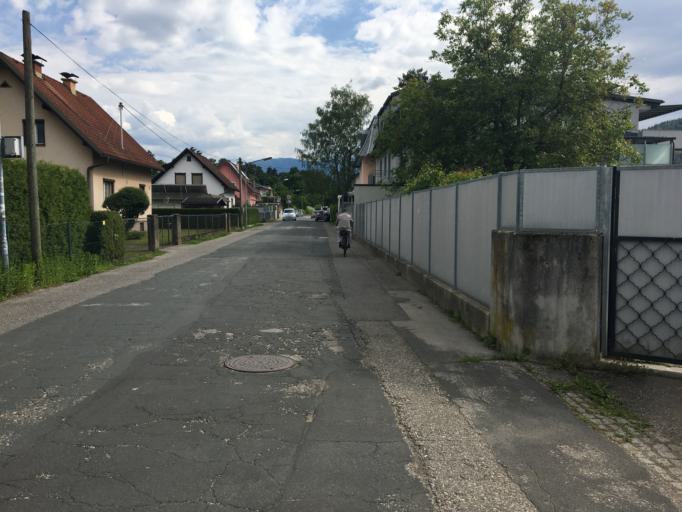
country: AT
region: Carinthia
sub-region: Klagenfurt am Woerthersee
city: Klagenfurt am Woerthersee
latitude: 46.6109
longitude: 14.2709
